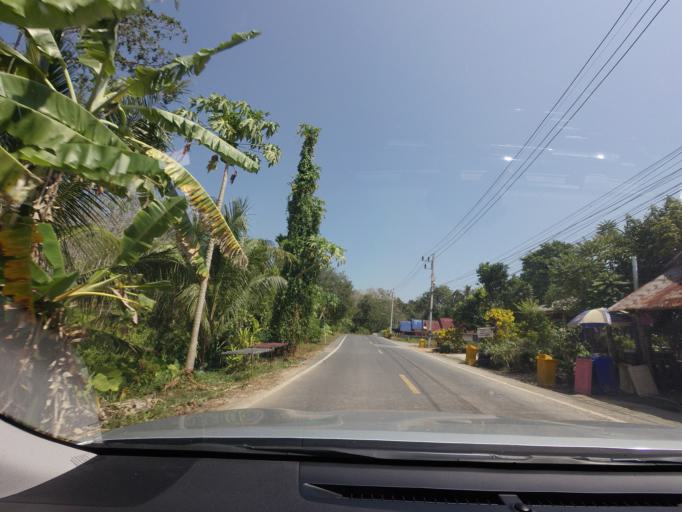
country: TH
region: Phangnga
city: Takua Thung
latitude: 8.2532
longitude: 98.4153
